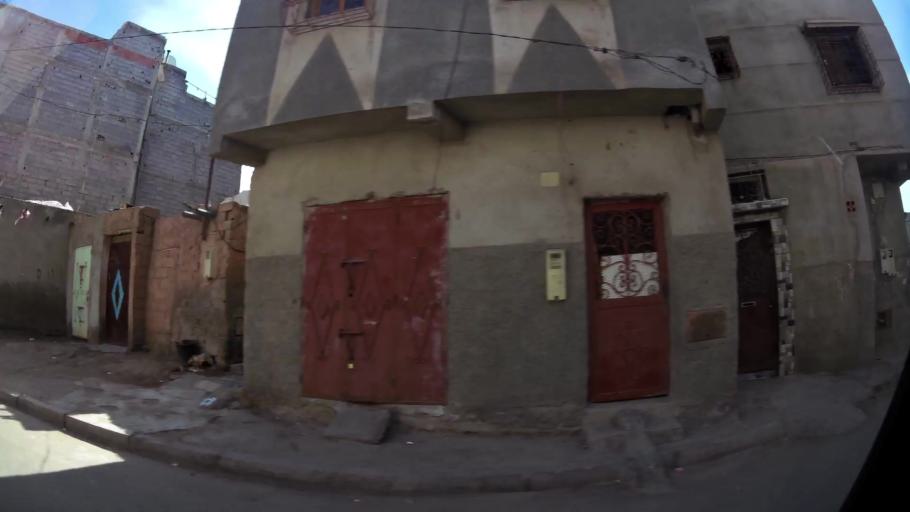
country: MA
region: Marrakech-Tensift-Al Haouz
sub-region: Marrakech
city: Marrakesh
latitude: 31.6377
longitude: -7.9772
